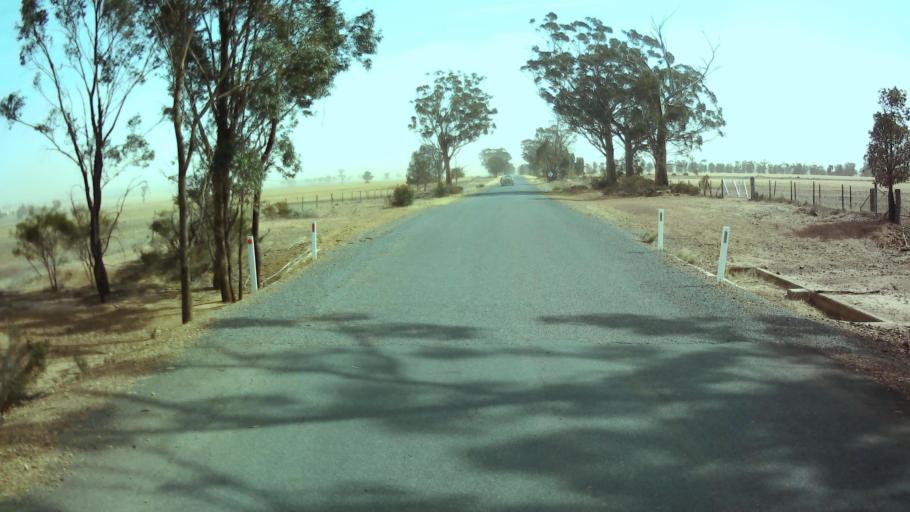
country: AU
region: New South Wales
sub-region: Weddin
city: Grenfell
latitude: -33.7734
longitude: 147.9863
